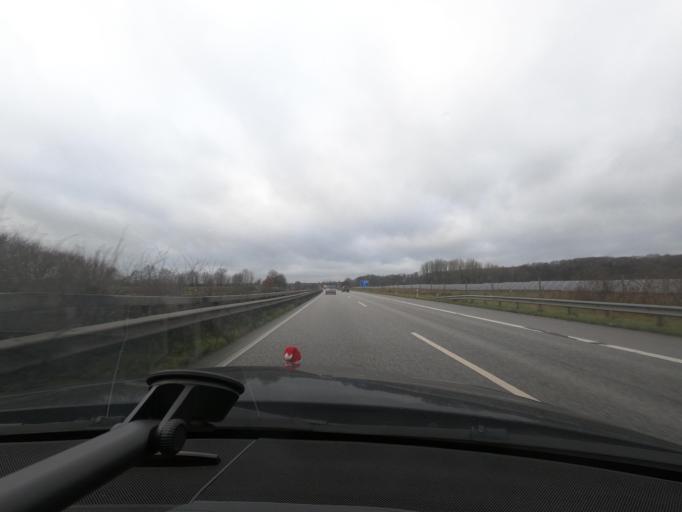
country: DE
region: Schleswig-Holstein
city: Datgen
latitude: 54.1845
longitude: 9.9415
